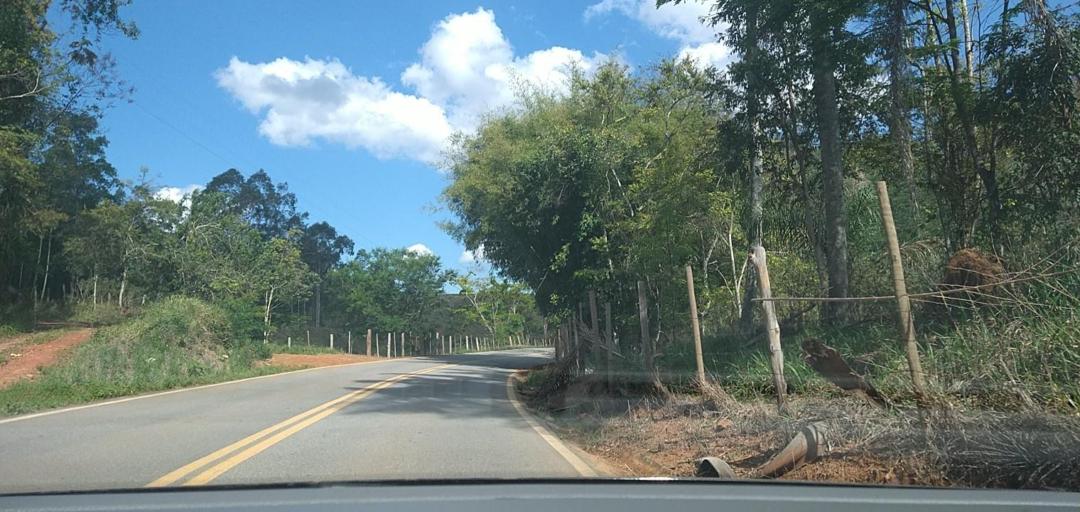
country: BR
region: Minas Gerais
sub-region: Rio Piracicaba
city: Rio Piracicaba
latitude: -19.9969
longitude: -43.1099
